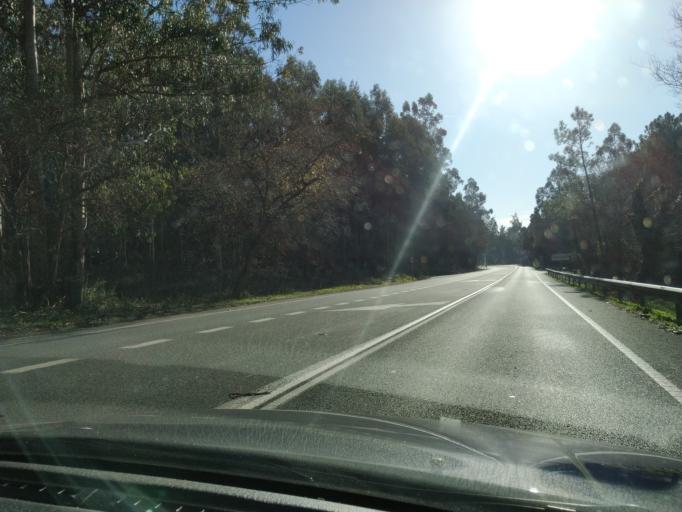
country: ES
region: Galicia
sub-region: Provincia da Coruna
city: Vedra
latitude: 42.7924
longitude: -8.4599
